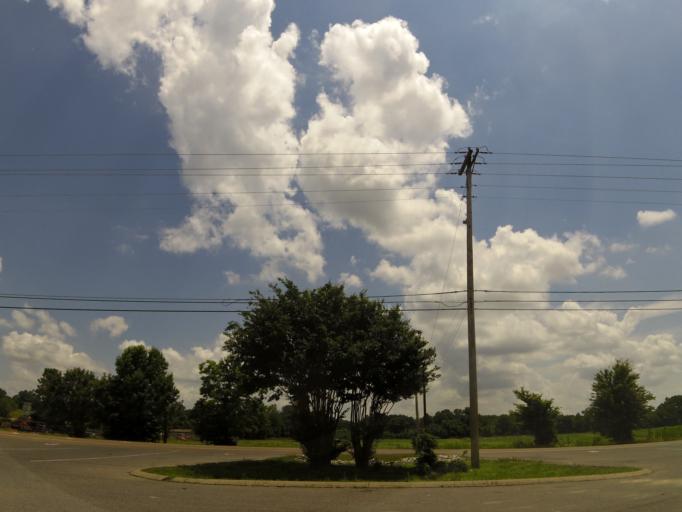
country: US
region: Tennessee
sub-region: Dyer County
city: Dyersburg
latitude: 36.0254
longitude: -89.3428
